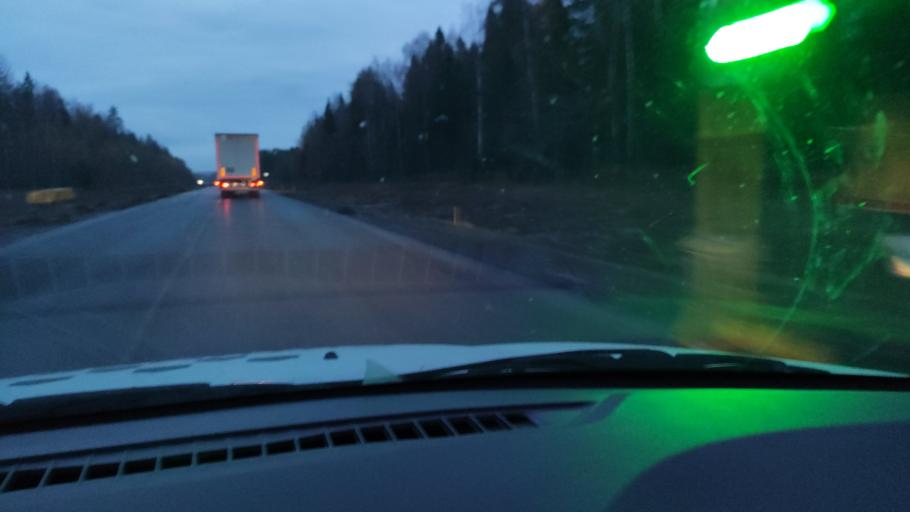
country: RU
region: Kirov
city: Kostino
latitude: 58.8224
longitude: 53.3600
